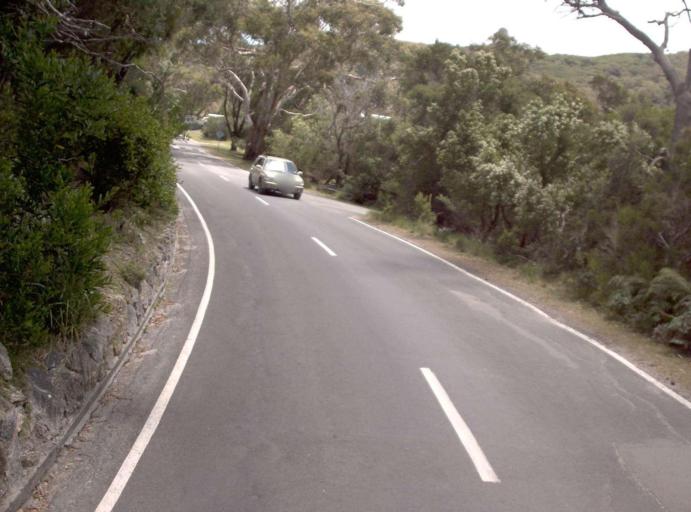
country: AU
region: Victoria
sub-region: Latrobe
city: Morwell
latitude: -39.0305
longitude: 146.3240
